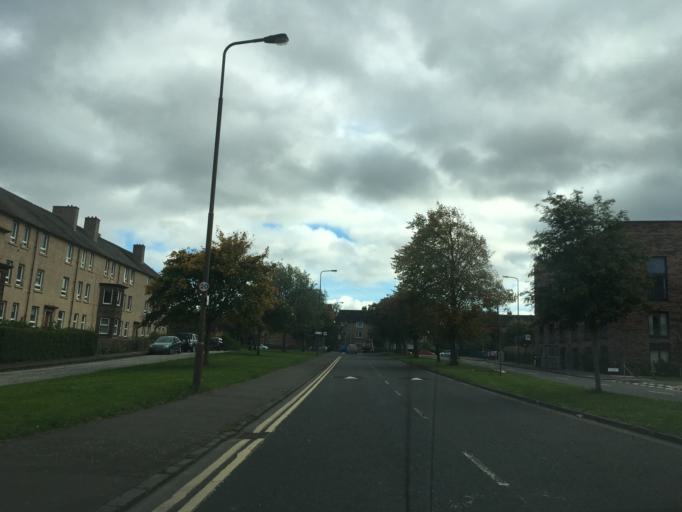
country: GB
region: Scotland
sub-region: Edinburgh
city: Edinburgh
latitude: 55.9684
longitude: -3.2495
